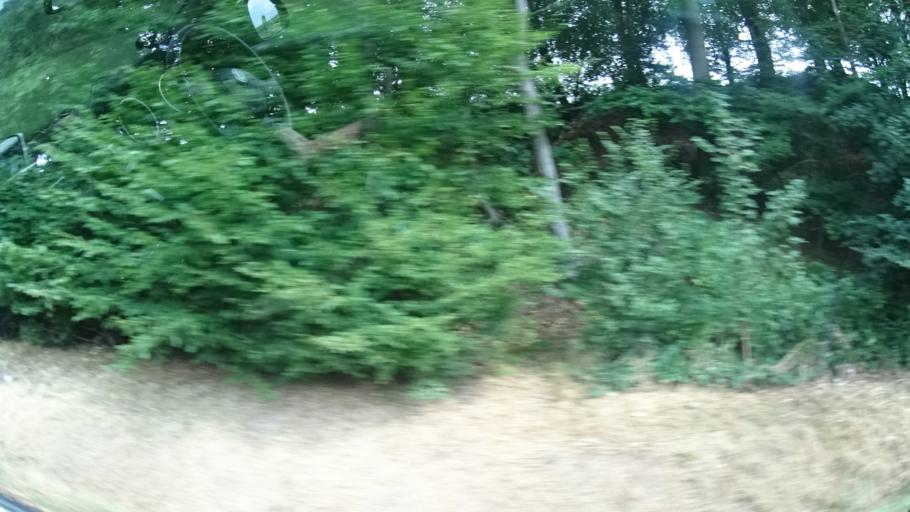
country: DE
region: Hesse
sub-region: Regierungsbezirk Kassel
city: Niederaula
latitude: 50.7820
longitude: 9.6051
